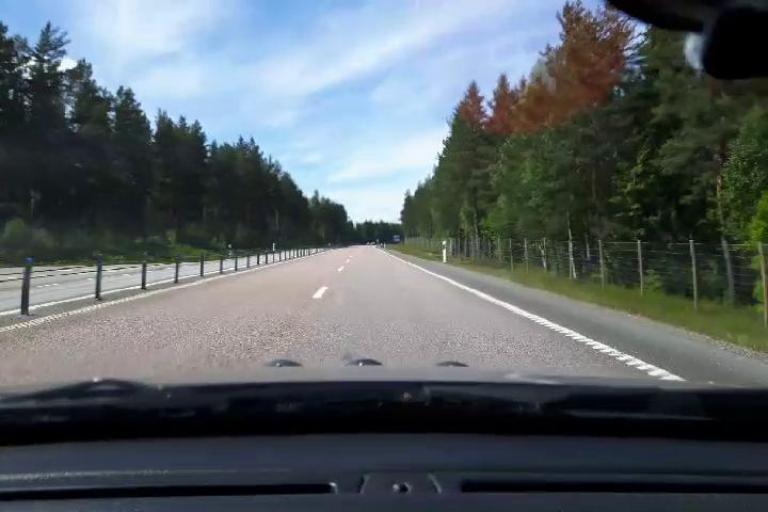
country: SE
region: Gaevleborg
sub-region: Gavle Kommun
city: Norrsundet
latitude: 60.9940
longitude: 16.9993
